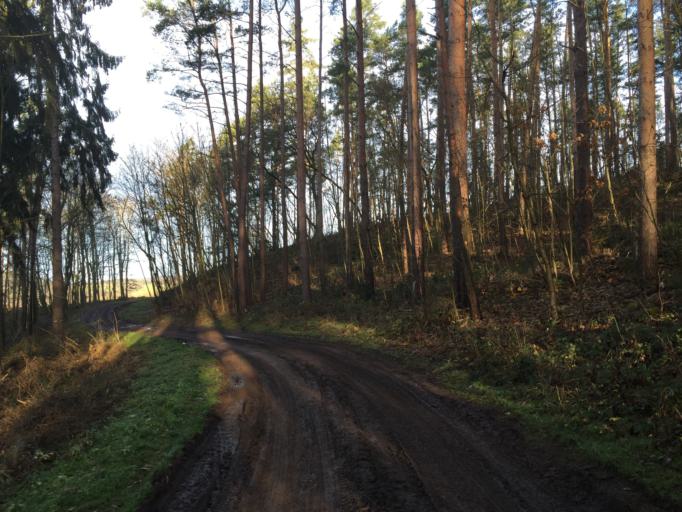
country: DE
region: Thuringia
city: Eichenberg
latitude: 50.7853
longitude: 11.5334
